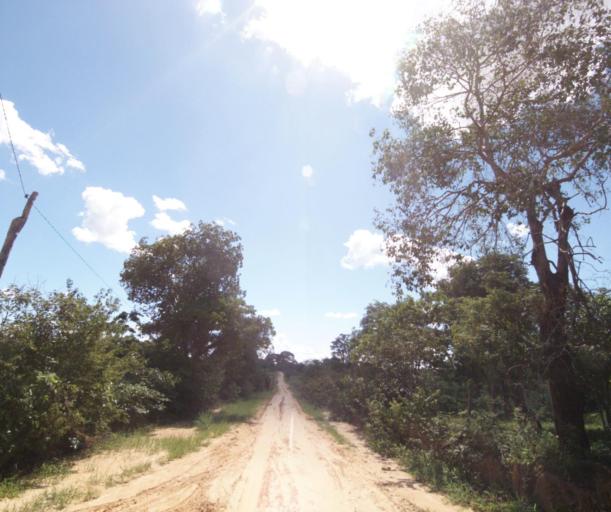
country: BR
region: Bahia
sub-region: Carinhanha
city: Carinhanha
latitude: -14.2344
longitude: -44.3129
